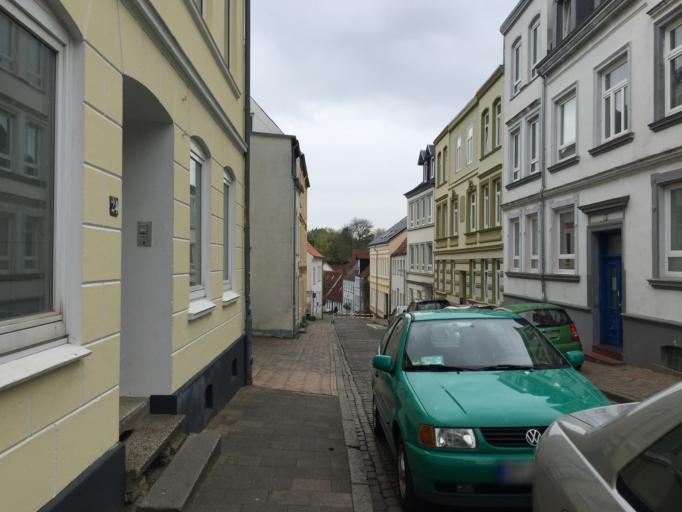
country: DE
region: Schleswig-Holstein
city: Flensburg
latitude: 54.7813
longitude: 9.4459
